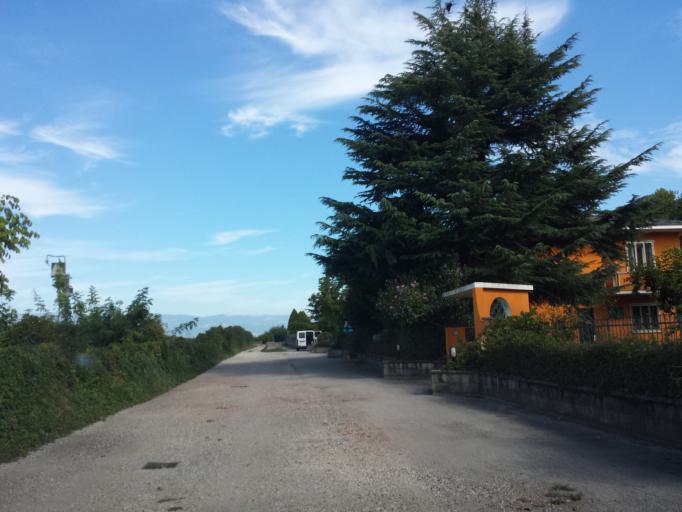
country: IT
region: Veneto
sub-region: Provincia di Vicenza
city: Monticello Conte Otto
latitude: 45.5696
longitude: 11.5686
